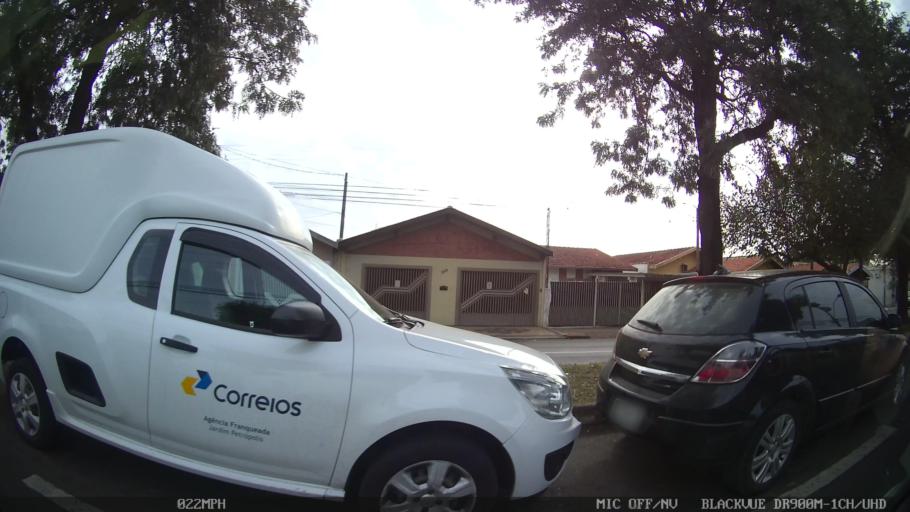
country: BR
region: Sao Paulo
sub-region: Piracicaba
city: Piracicaba
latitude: -22.7371
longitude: -47.6237
